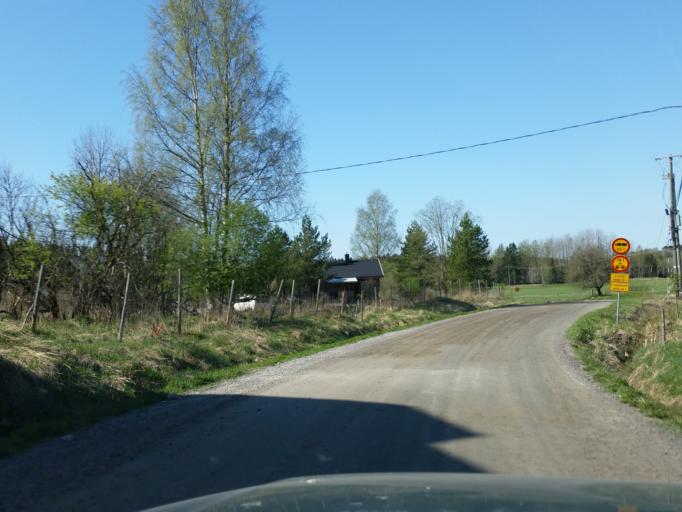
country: FI
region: Uusimaa
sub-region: Helsinki
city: Karjalohja
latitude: 60.1440
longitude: 23.7706
